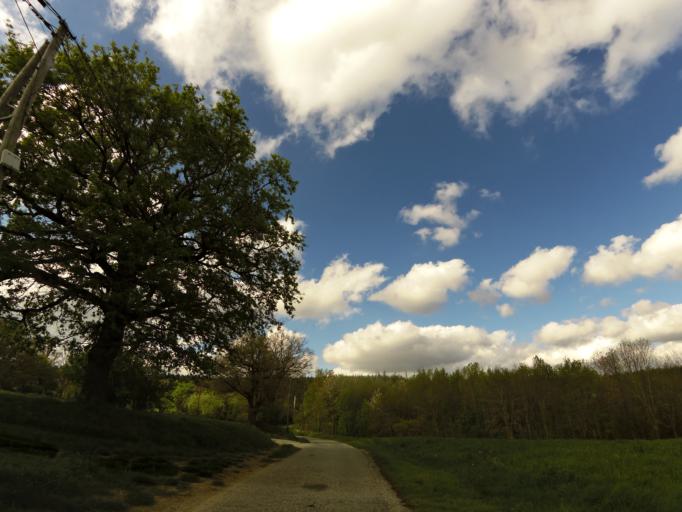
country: FR
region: Midi-Pyrenees
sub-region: Departement du Tarn
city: Soreze
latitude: 43.3745
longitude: 2.0655
